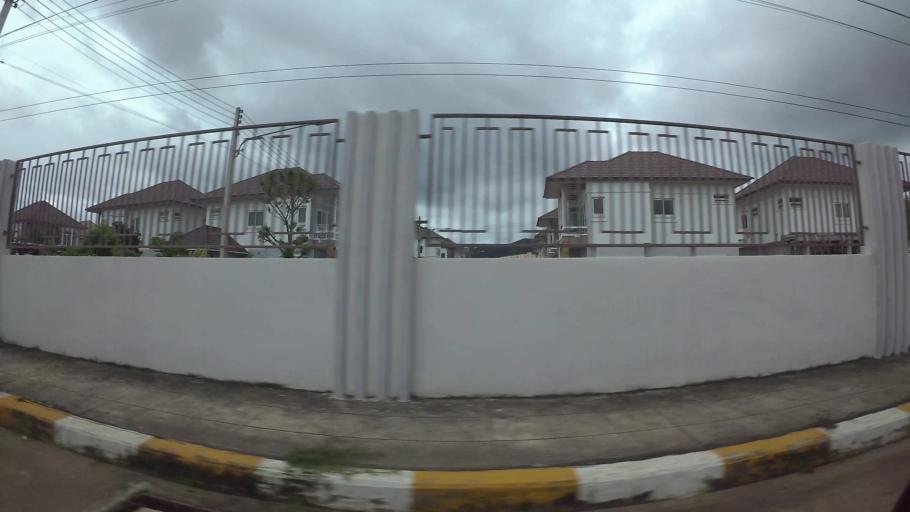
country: TH
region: Chon Buri
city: Sattahip
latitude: 12.7268
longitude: 100.8934
